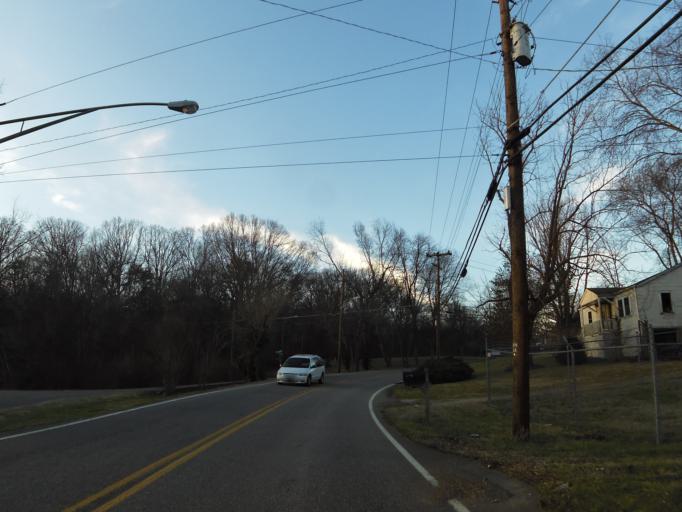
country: US
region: Tennessee
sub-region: Knox County
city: Knoxville
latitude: 36.0149
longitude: -83.8690
